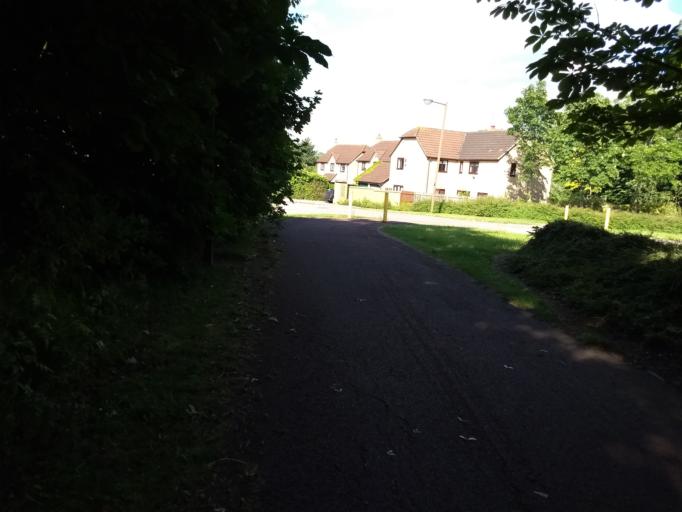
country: GB
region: England
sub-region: Milton Keynes
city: Shenley Church End
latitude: 52.0289
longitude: -0.7908
